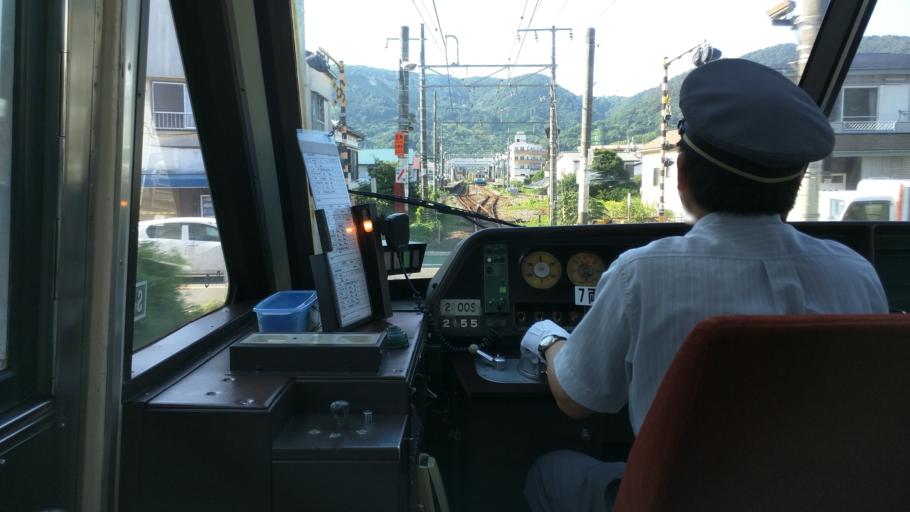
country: JP
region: Shizuoka
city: Ito
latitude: 35.0040
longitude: 139.0801
